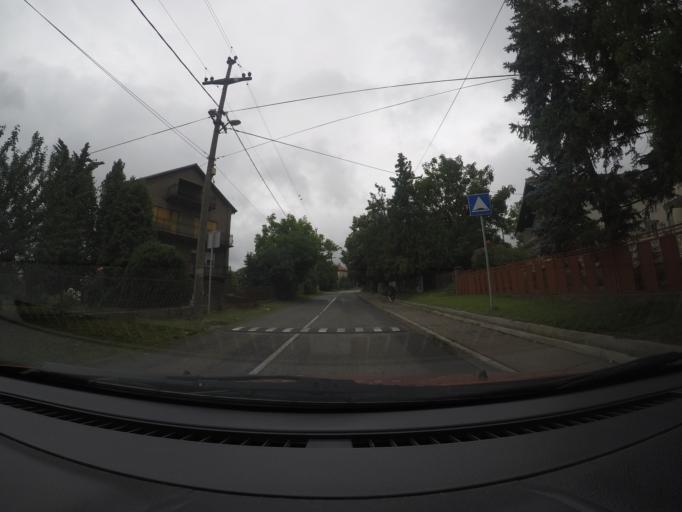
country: RS
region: Central Serbia
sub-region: Belgrade
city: Zvezdara
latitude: 44.6984
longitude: 20.5568
